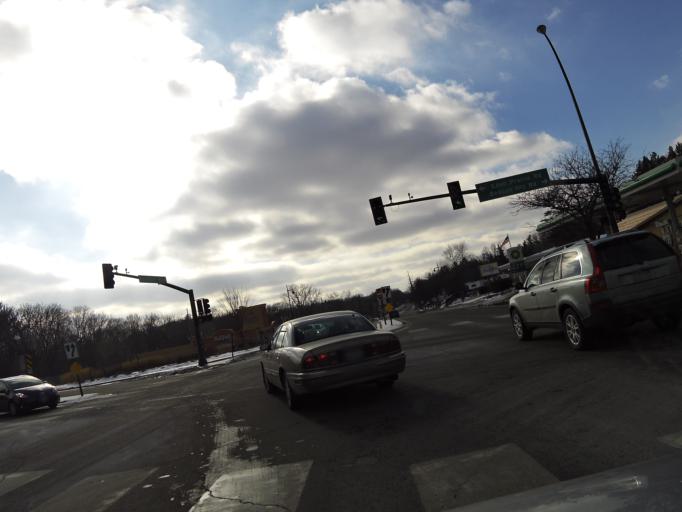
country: US
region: Minnesota
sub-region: Hennepin County
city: Hopkins
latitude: 44.9047
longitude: -93.4650
